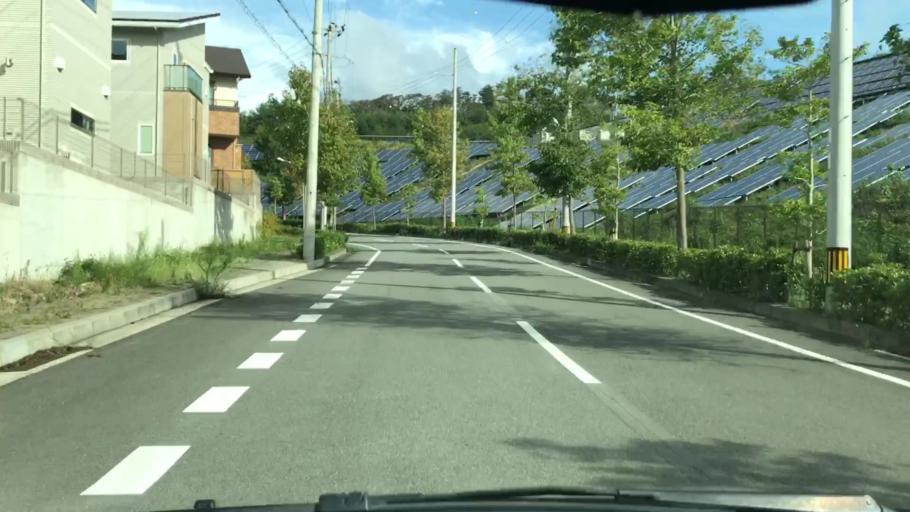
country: JP
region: Hyogo
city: Takarazuka
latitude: 34.8377
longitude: 135.3117
